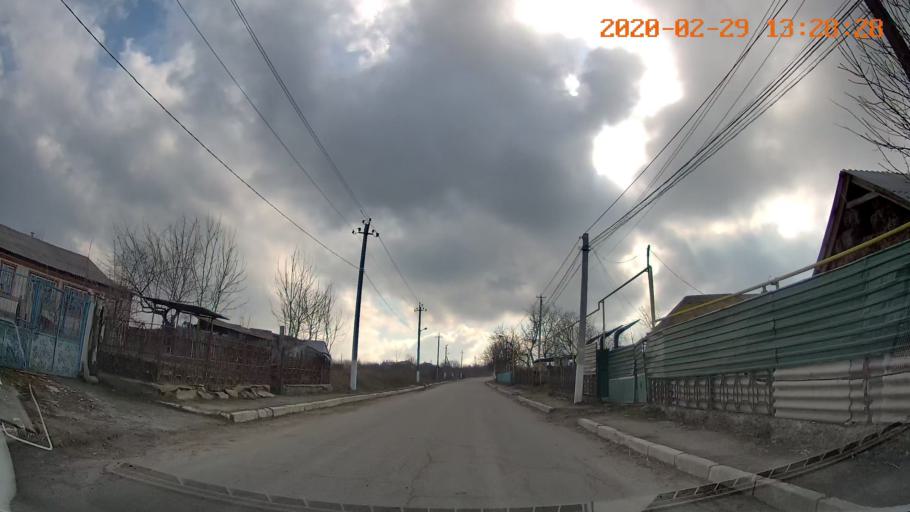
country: MD
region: Telenesti
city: Camenca
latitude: 47.9052
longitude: 28.6423
